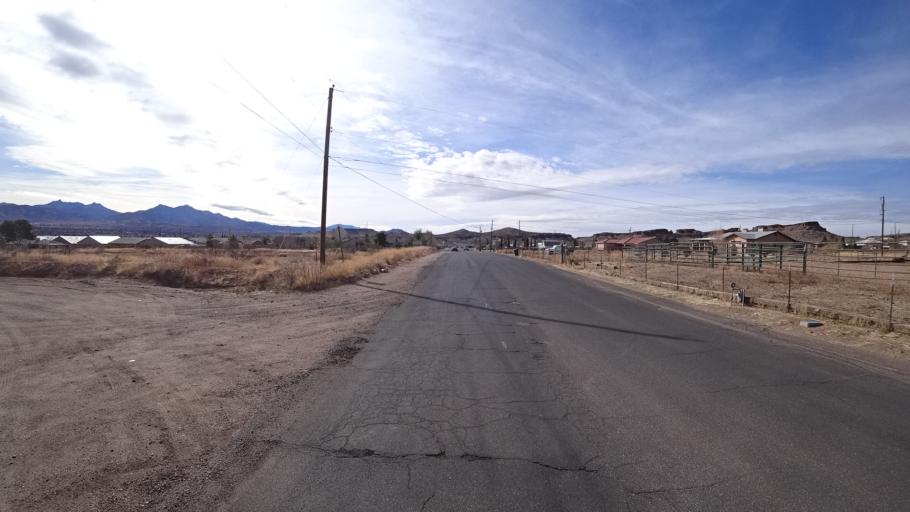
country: US
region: Arizona
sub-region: Mohave County
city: Kingman
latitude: 35.2212
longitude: -114.0492
